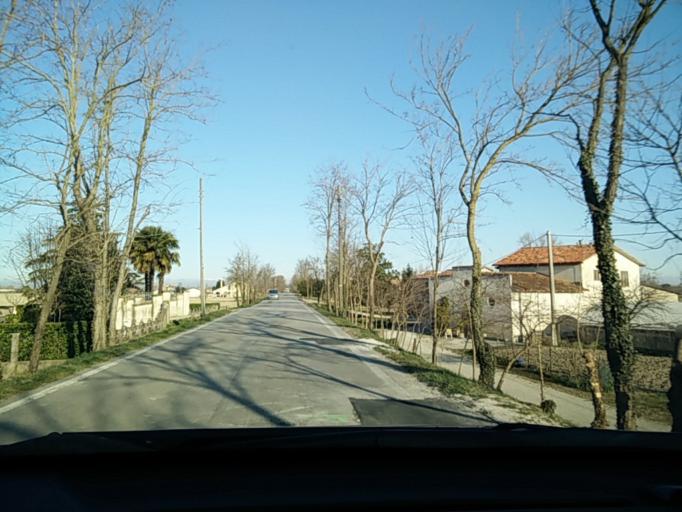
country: IT
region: Veneto
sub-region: Provincia di Venezia
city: Passarella
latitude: 45.5845
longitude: 12.6116
